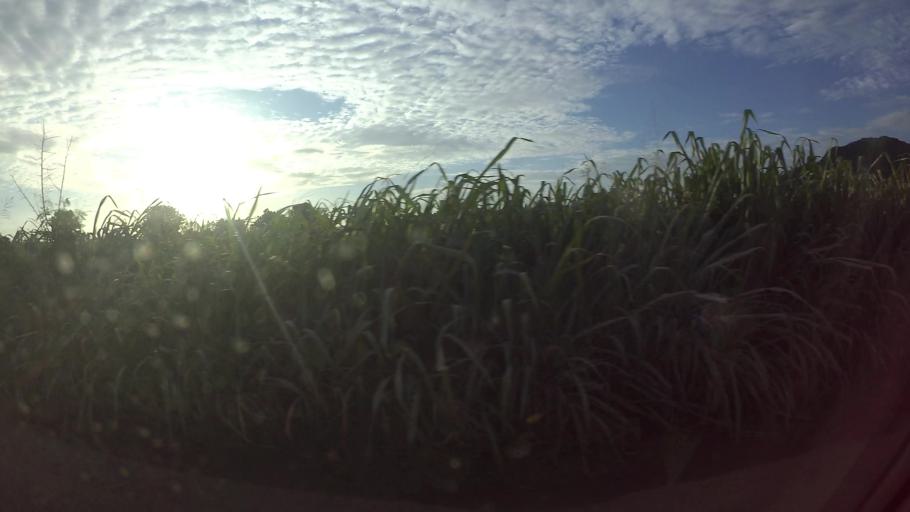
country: TH
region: Chon Buri
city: Sattahip
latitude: 12.7506
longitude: 100.9405
